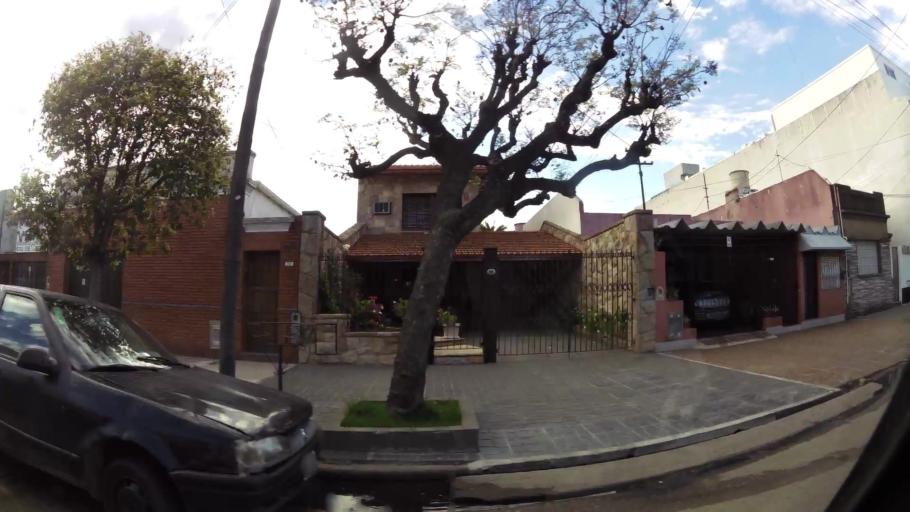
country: AR
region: Buenos Aires
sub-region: Partido de Avellaneda
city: Avellaneda
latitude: -34.6855
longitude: -58.3504
